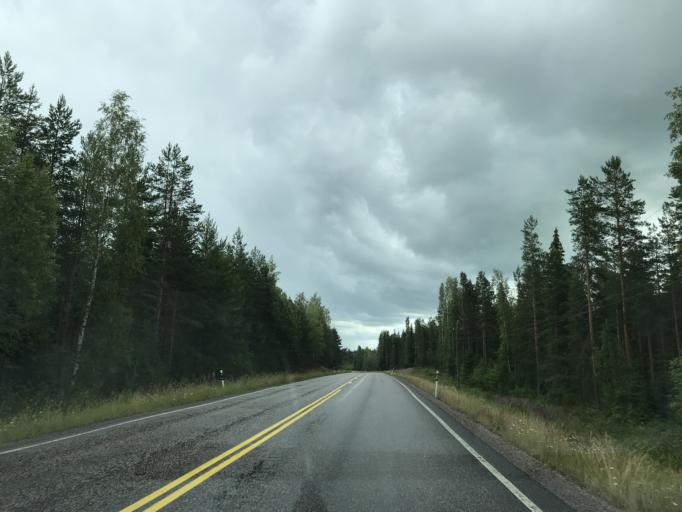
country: FI
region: Paijanne Tavastia
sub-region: Lahti
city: Orimattila
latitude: 60.7851
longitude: 25.6143
